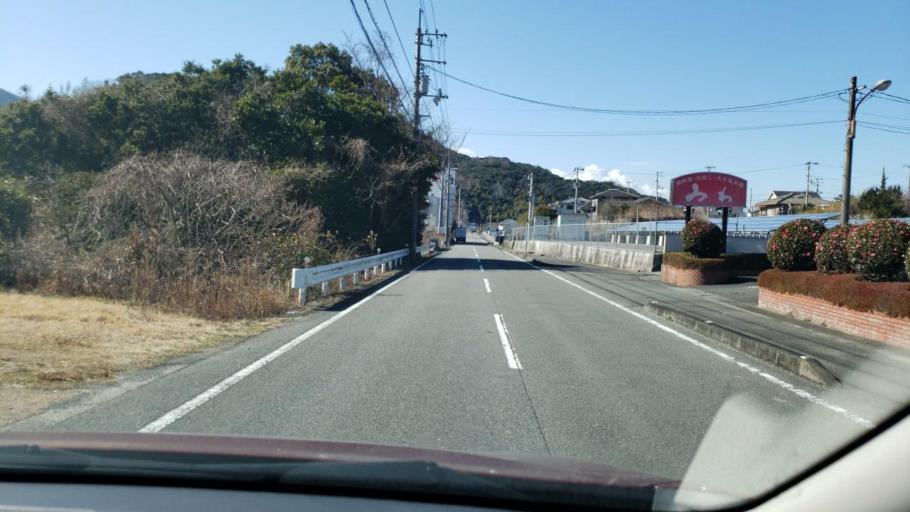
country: JP
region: Tokushima
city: Narutocho-mitsuishi
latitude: 34.2205
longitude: 134.5645
